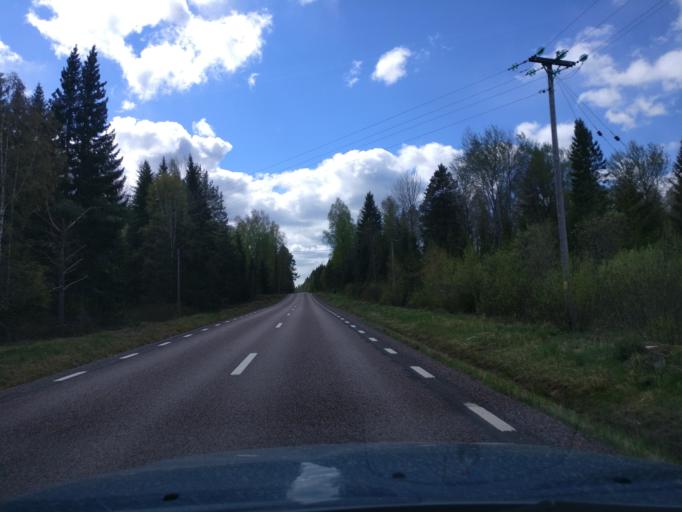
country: SE
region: Vaermland
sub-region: Karlstads Kommun
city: Molkom
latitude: 59.7538
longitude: 13.6895
